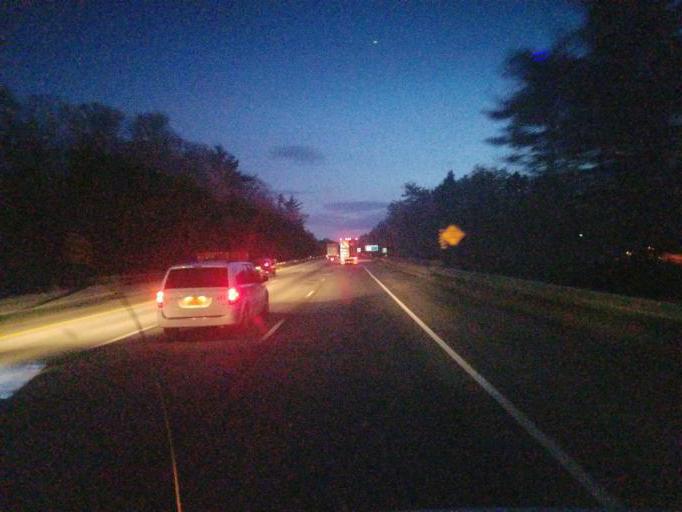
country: US
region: Massachusetts
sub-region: Middlesex County
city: Hudson
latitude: 42.3712
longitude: -71.5958
